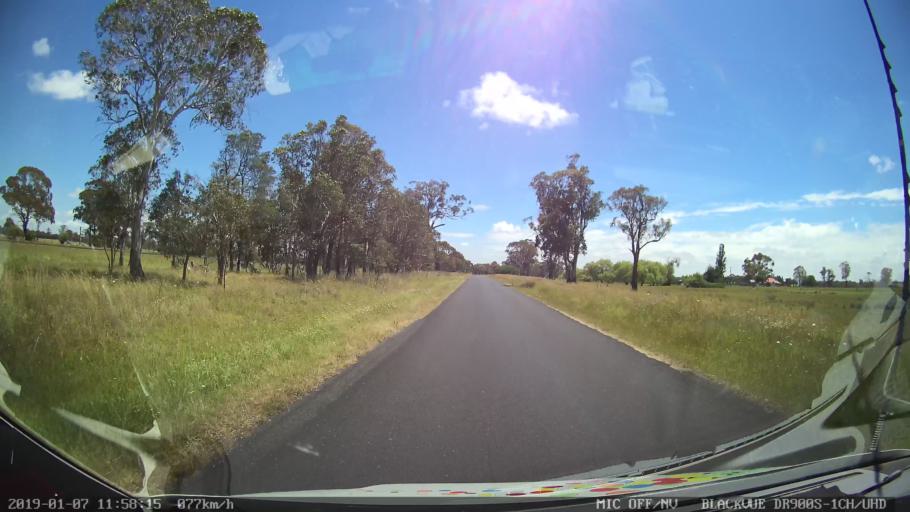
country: AU
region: New South Wales
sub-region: Guyra
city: Guyra
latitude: -30.2554
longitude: 151.6674
